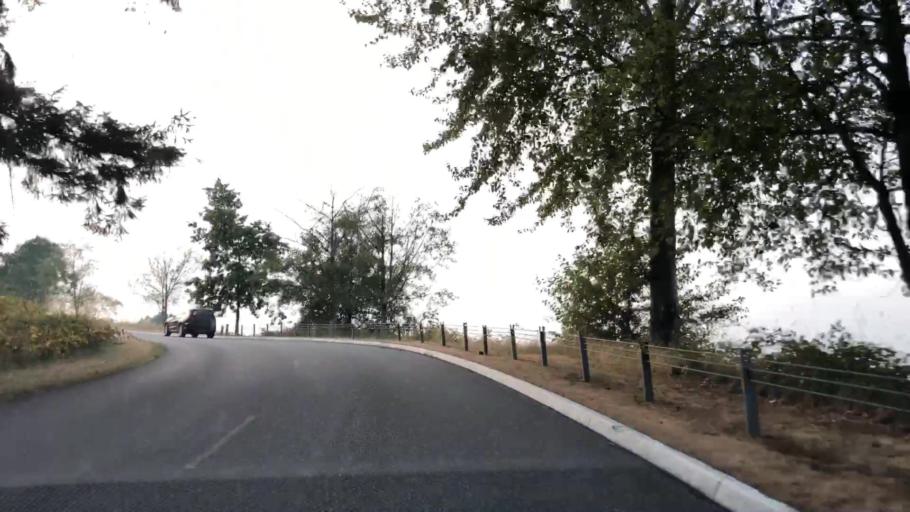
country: US
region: Washington
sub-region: King County
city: Newcastle
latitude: 47.5363
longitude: -122.1369
